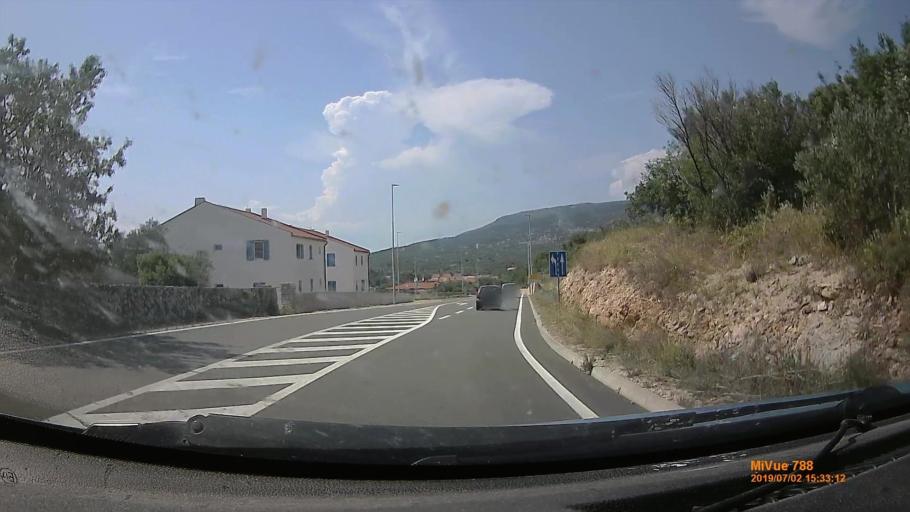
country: HR
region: Primorsko-Goranska
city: Cres
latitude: 44.9577
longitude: 14.4159
